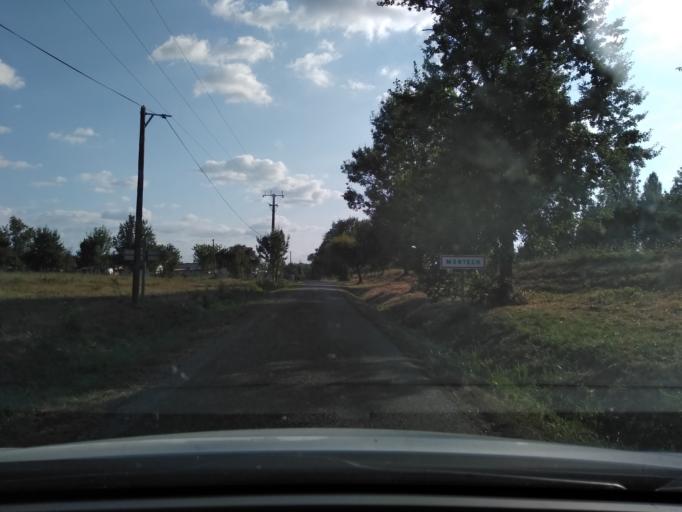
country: FR
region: Midi-Pyrenees
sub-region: Departement du Tarn-et-Garonne
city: Montech
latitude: 43.9695
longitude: 1.2439
